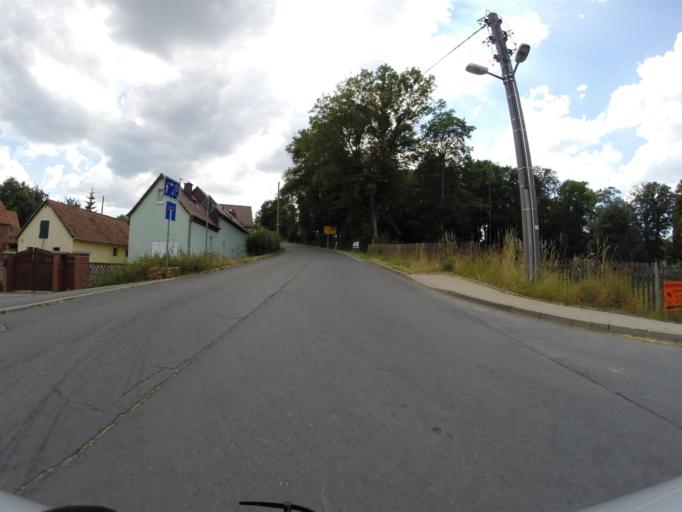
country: DE
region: Thuringia
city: Schloben
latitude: 50.8923
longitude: 11.6912
